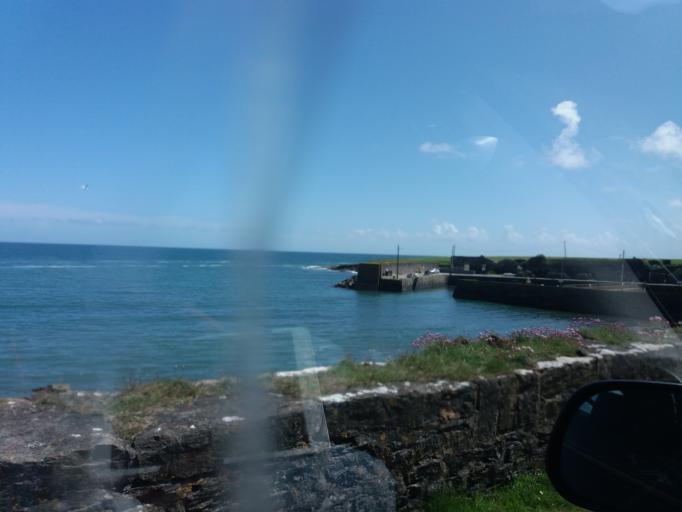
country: IE
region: Munster
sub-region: Waterford
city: Dunmore East
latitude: 52.1353
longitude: -6.9105
